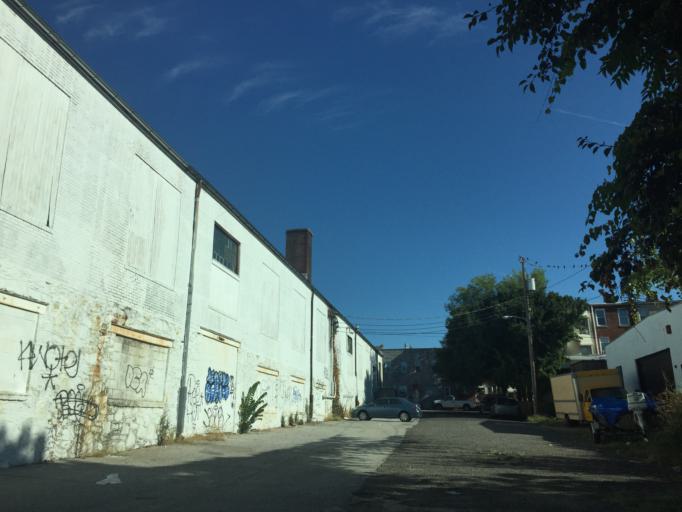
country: US
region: Maryland
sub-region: City of Baltimore
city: Baltimore
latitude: 39.3143
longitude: -76.6229
